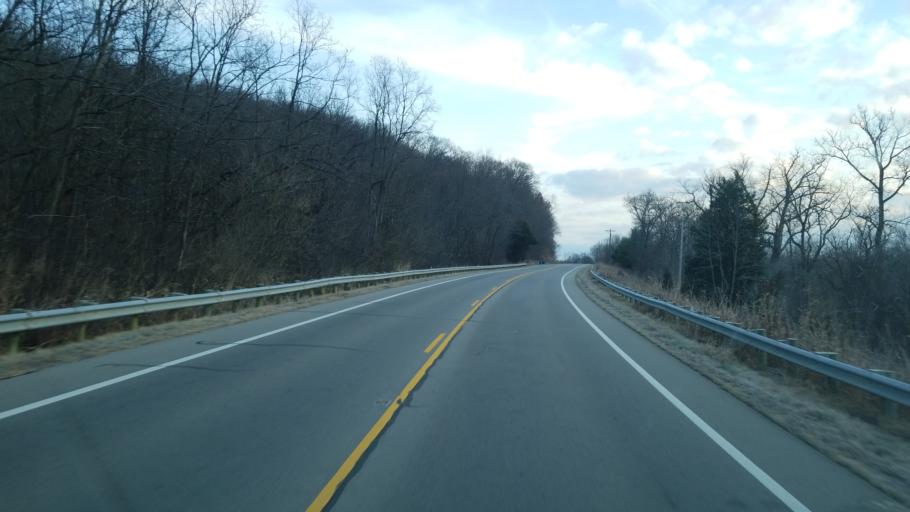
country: US
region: Ohio
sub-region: Ross County
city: Frankfort
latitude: 39.2996
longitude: -83.1403
